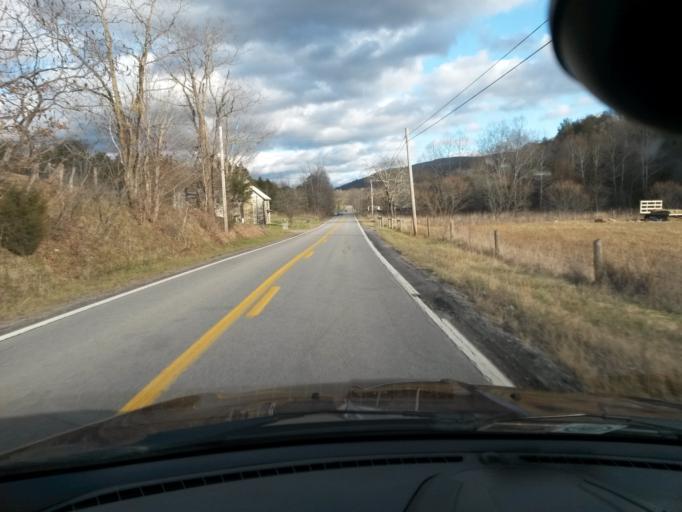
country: US
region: West Virginia
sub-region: Monroe County
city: Union
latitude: 37.4779
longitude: -80.6402
